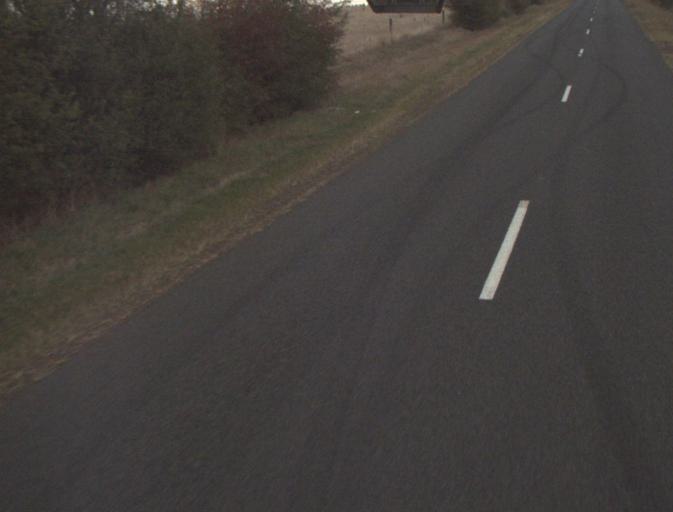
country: AU
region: Tasmania
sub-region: Northern Midlands
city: Evandale
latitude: -41.5135
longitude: 147.2133
